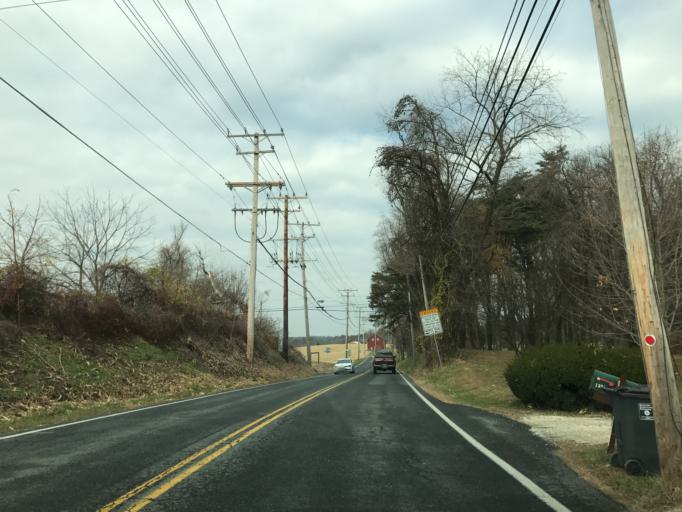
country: US
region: Maryland
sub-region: Harford County
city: Jarrettsville
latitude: 39.5943
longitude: -76.4389
